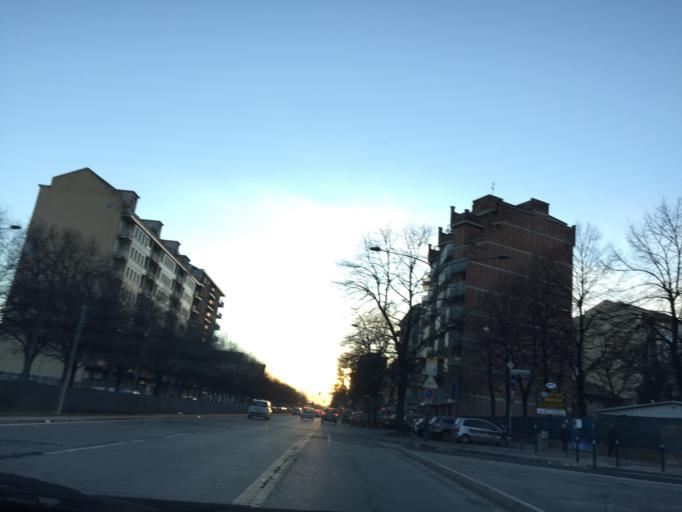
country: IT
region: Piedmont
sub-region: Provincia di Torino
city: Gerbido
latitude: 45.0391
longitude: 7.6317
